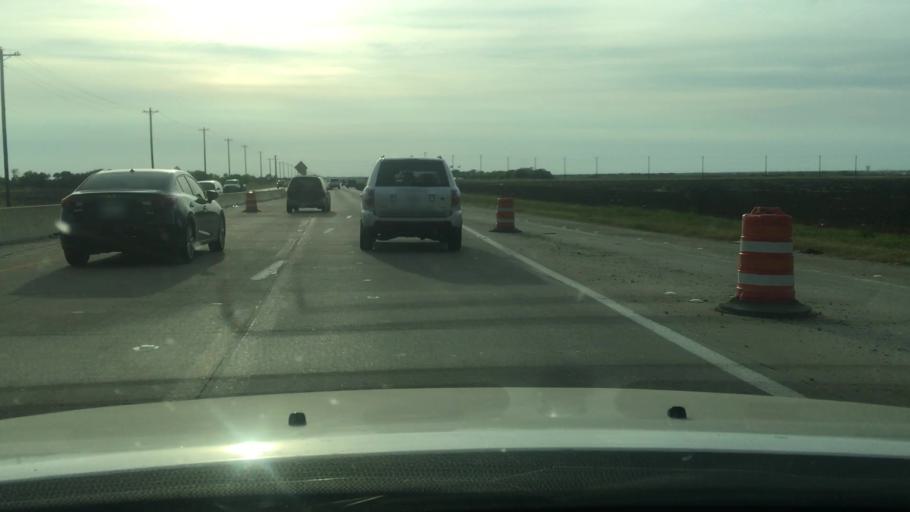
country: US
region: Texas
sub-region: Collin County
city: Prosper
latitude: 33.2194
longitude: -96.8401
